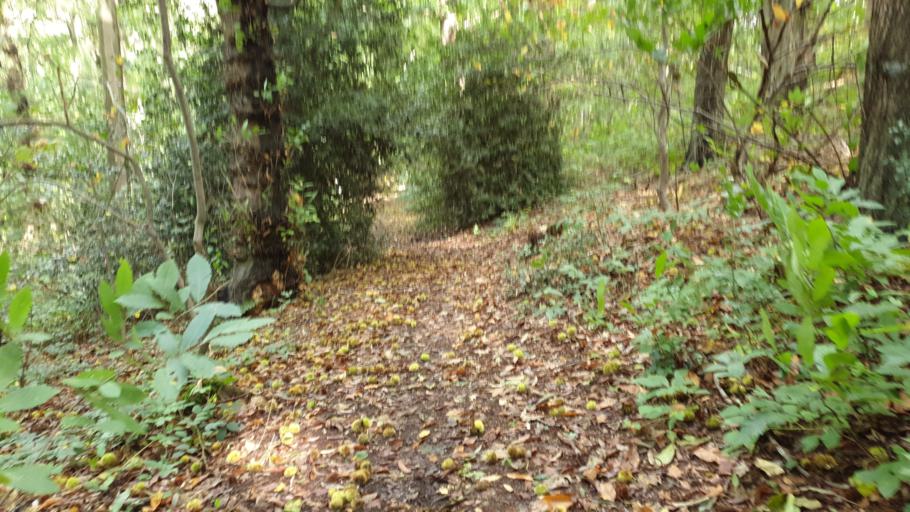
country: FR
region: Haute-Normandie
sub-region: Departement de la Seine-Maritime
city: Saint-Laurent-de-Brevedent
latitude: 49.5307
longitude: 0.2595
